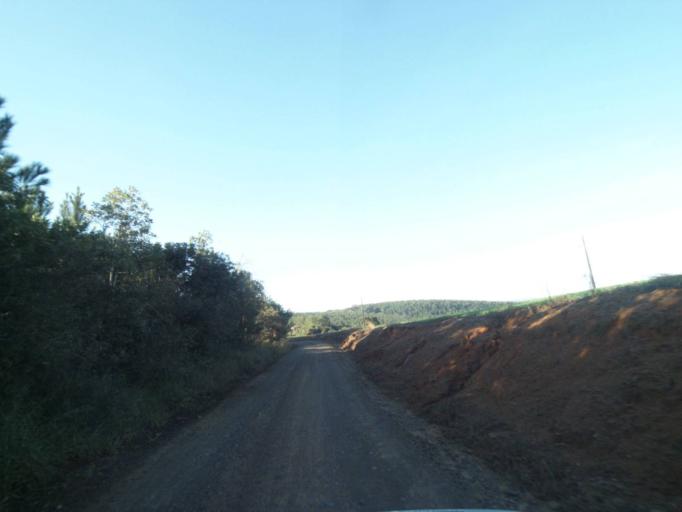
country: BR
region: Parana
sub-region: Telemaco Borba
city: Telemaco Borba
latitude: -24.4306
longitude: -50.5976
